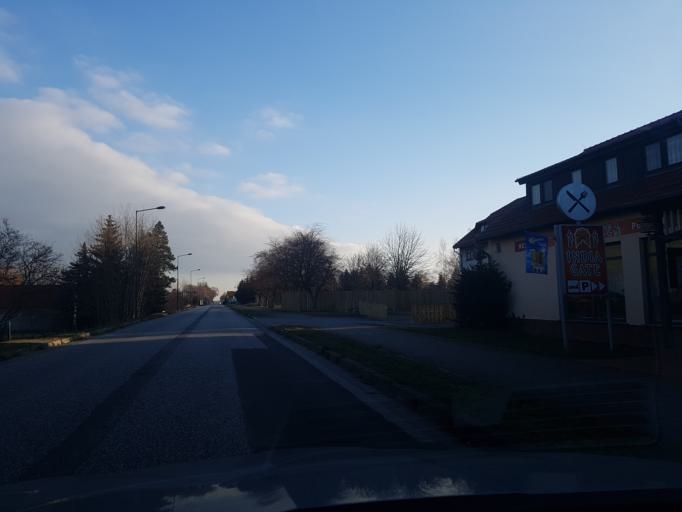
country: DE
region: Brandenburg
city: Luckau
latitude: 51.8316
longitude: 13.6380
